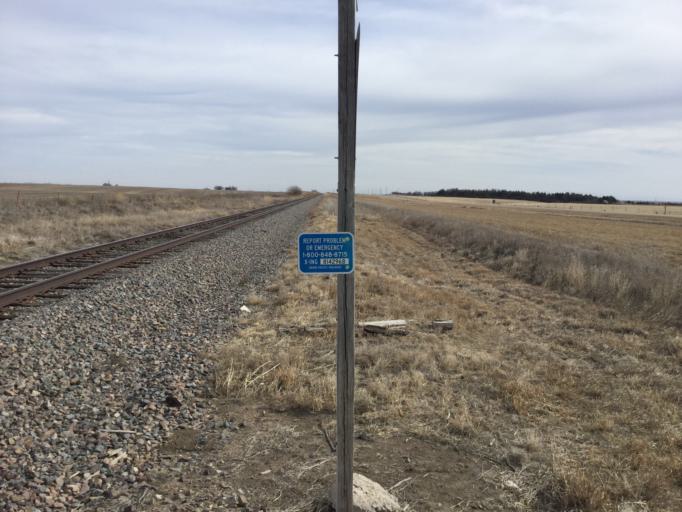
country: US
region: Kansas
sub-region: Ellis County
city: Victoria
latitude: 38.8447
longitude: -99.1884
